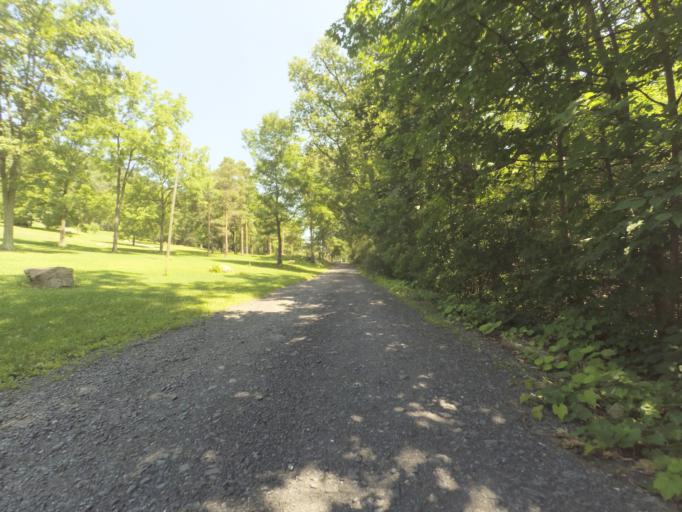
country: US
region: Pennsylvania
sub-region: Centre County
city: Pleasant Gap
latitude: 40.8275
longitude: -77.7335
